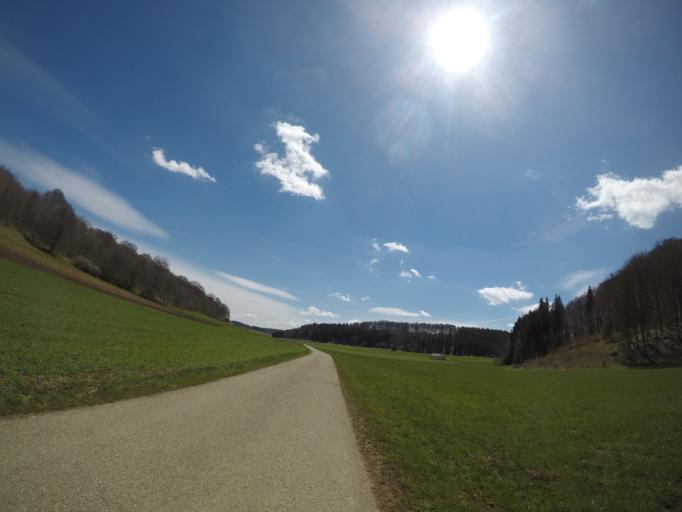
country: DE
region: Baden-Wuerttemberg
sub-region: Tuebingen Region
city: Westerheim
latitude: 48.5090
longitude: 9.6039
